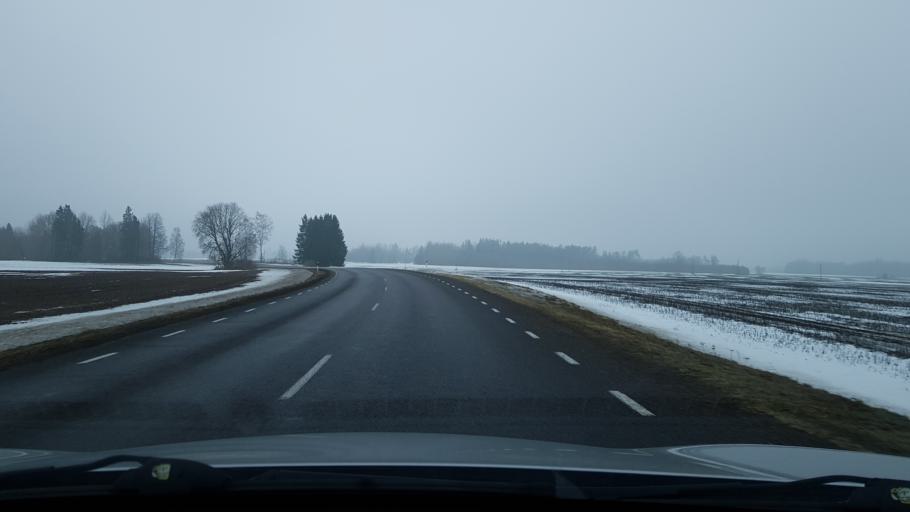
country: EE
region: Valgamaa
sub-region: Torva linn
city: Torva
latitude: 58.0928
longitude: 26.0114
